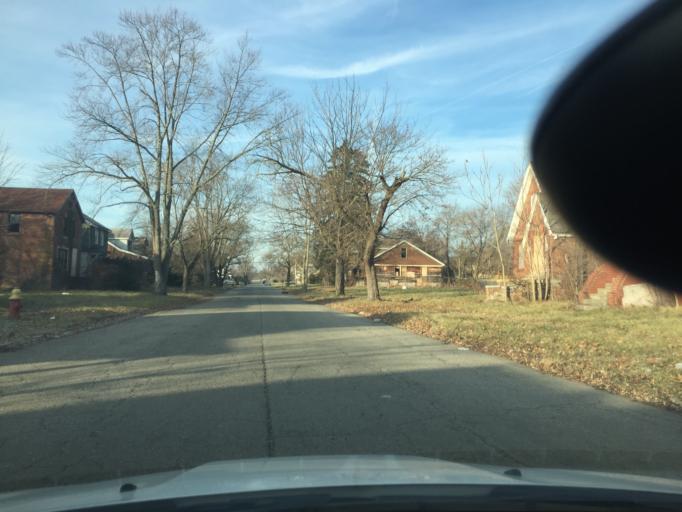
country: US
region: Michigan
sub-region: Macomb County
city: Eastpointe
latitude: 42.4394
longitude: -82.9671
